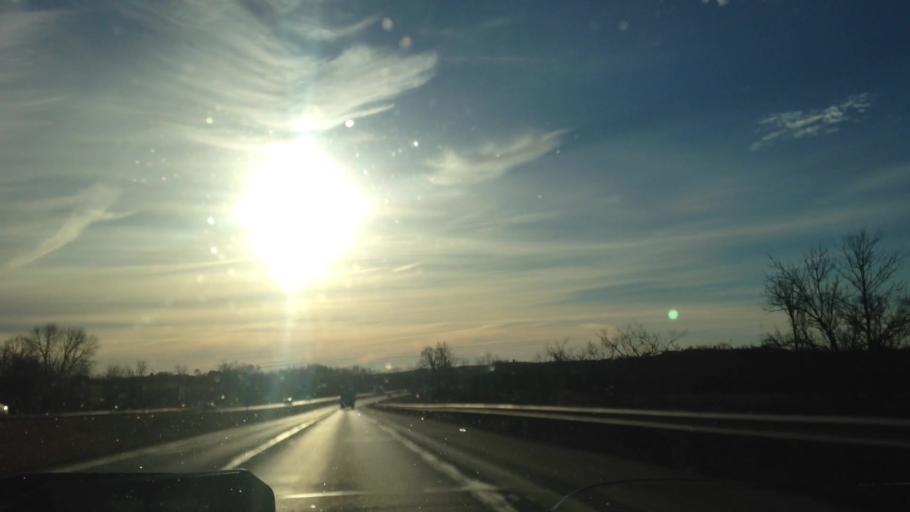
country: US
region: Wisconsin
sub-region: Dodge County
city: Theresa
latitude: 43.5131
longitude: -88.3741
